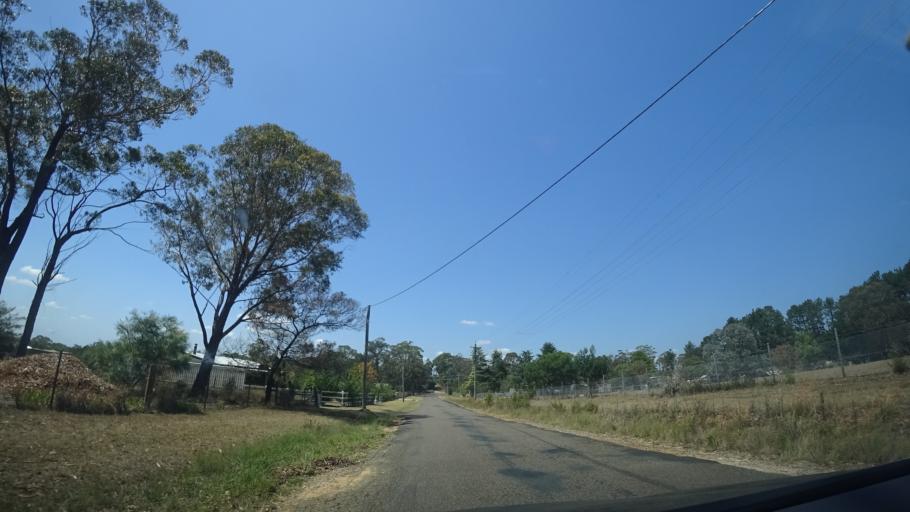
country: AU
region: New South Wales
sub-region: Wollondilly
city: Buxton
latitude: -34.2618
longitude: 150.5260
